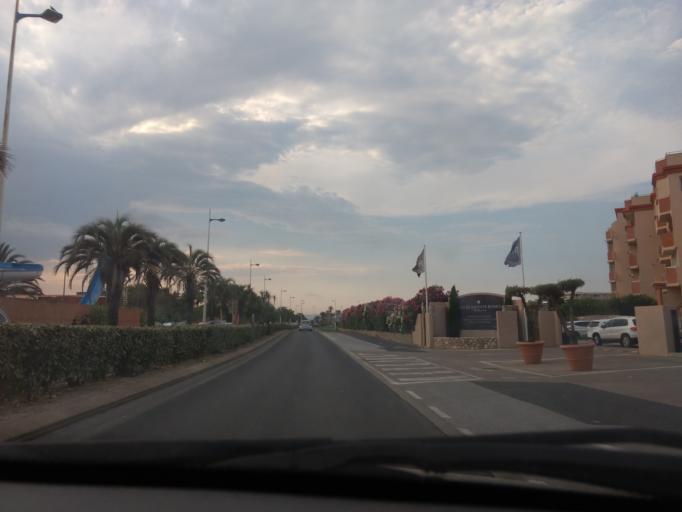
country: FR
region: Languedoc-Roussillon
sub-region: Departement des Pyrenees-Orientales
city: Canet-en-Roussillon
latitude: 42.6745
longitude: 3.0324
